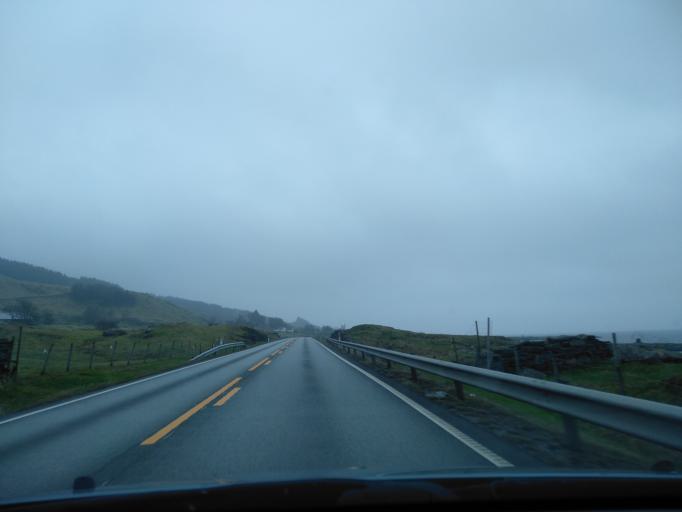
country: NO
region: Rogaland
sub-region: Rennesoy
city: Vikevag
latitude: 59.1204
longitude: 5.6888
